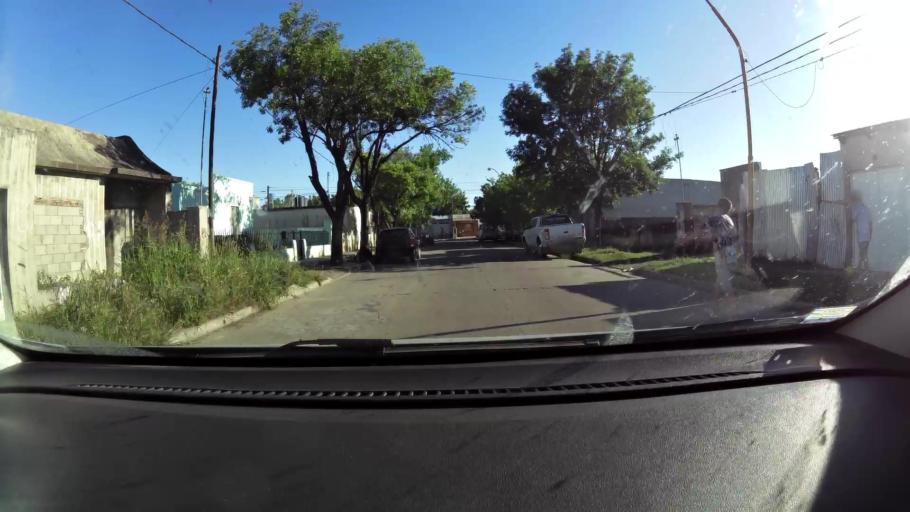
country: AR
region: Cordoba
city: San Francisco
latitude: -31.4404
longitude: -62.0918
